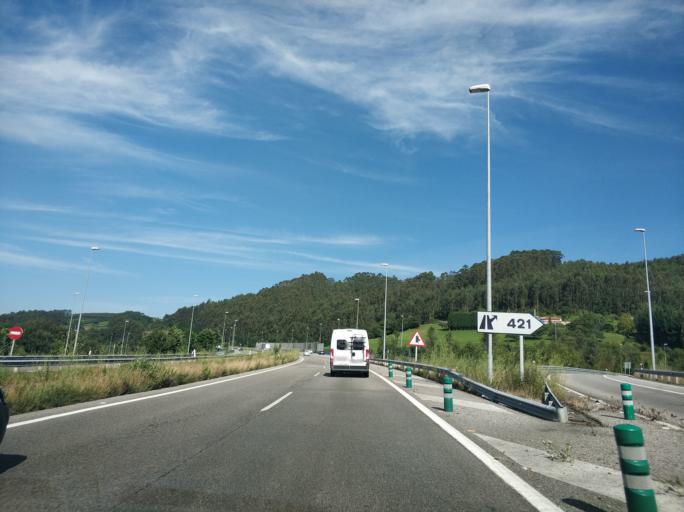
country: ES
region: Asturias
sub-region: Province of Asturias
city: Soto del Barco
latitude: 43.5191
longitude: -6.0677
